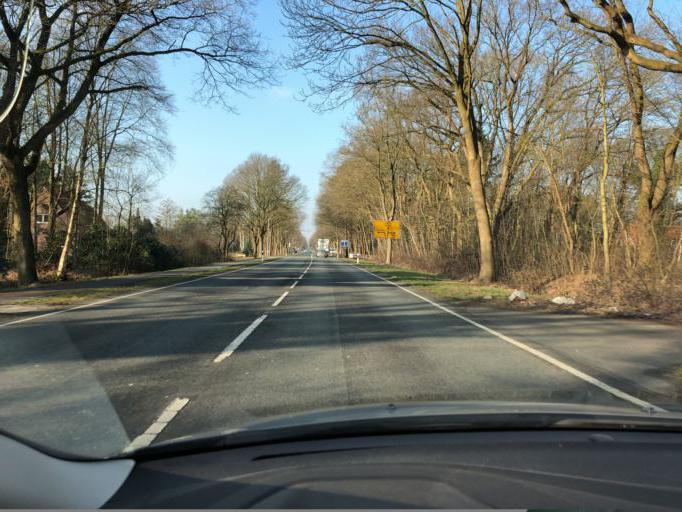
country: DE
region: Lower Saxony
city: Westerstede
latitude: 53.2931
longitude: 7.8683
